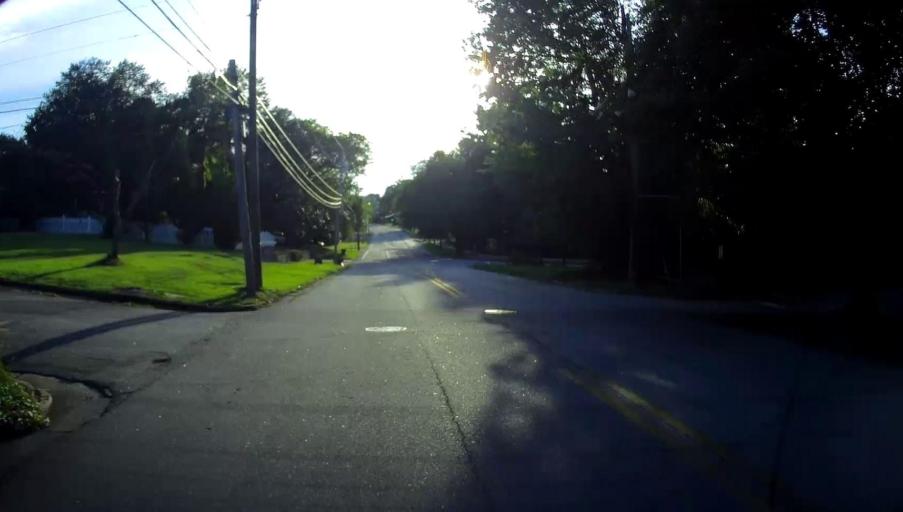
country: US
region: Georgia
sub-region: Muscogee County
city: Columbus
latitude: 32.4721
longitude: -84.9654
